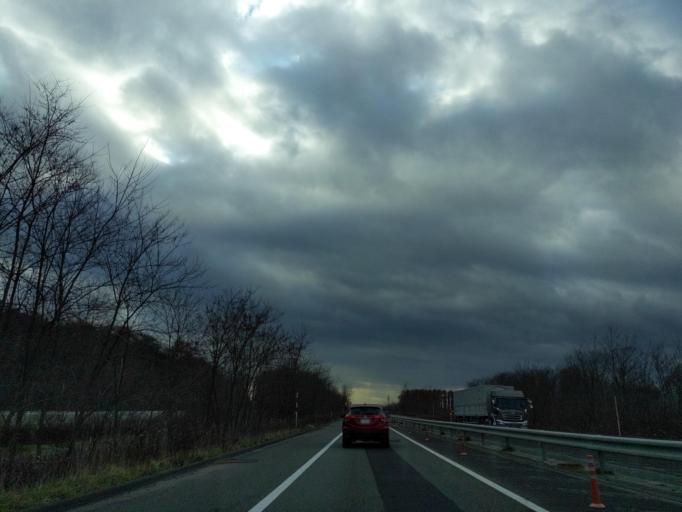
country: JP
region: Hokkaido
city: Chitose
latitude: 42.8479
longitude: 141.6991
